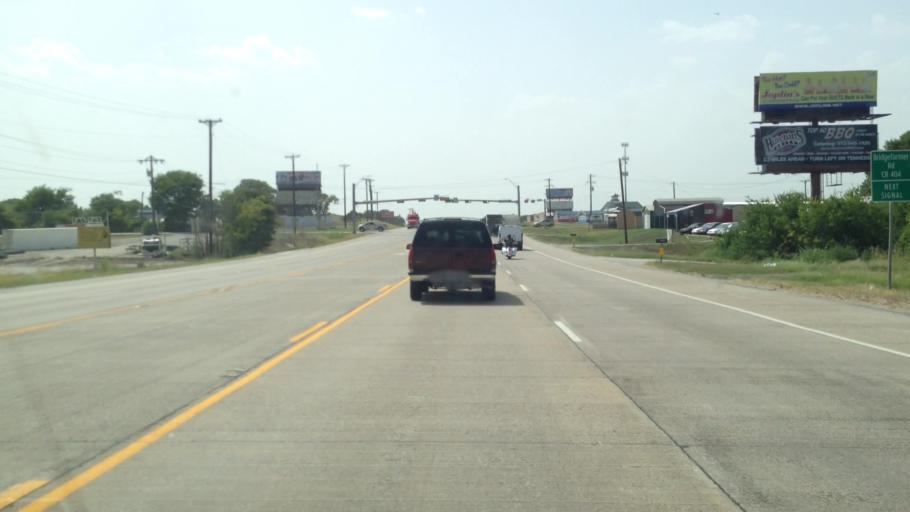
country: US
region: Texas
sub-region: Collin County
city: Lowry Crossing
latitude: 33.1888
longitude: -96.5459
